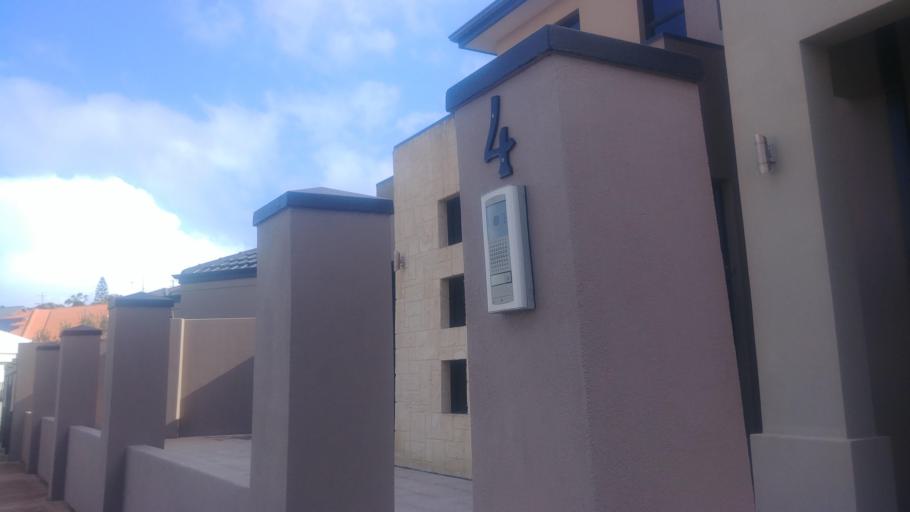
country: AU
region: Western Australia
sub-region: Fremantle
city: South Fremantle
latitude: -32.0680
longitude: 115.7640
